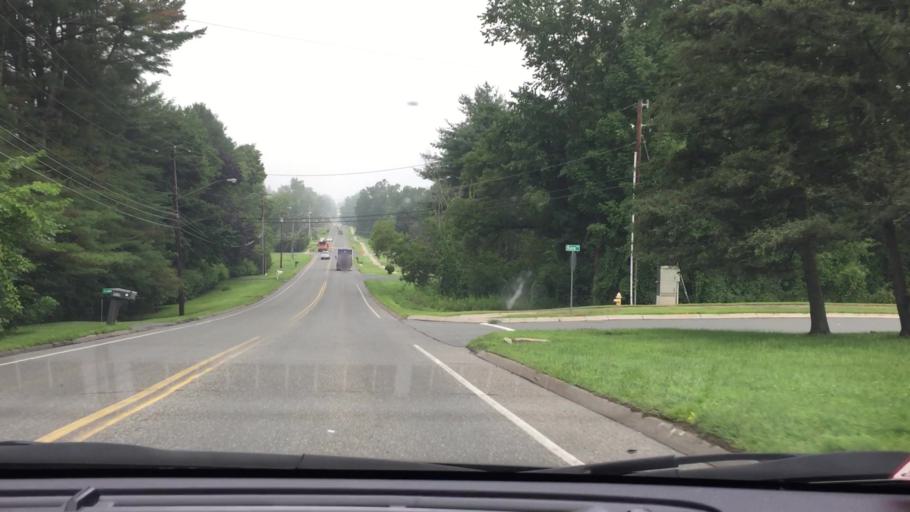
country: US
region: Massachusetts
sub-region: Berkshire County
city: Pittsfield
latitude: 42.4305
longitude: -73.2015
